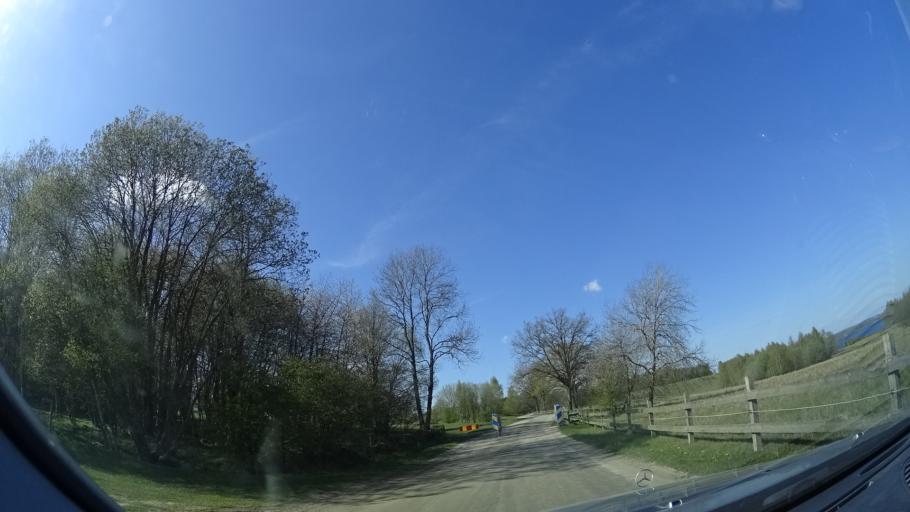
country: SE
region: Skane
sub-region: Hassleholms Kommun
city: Tormestorp
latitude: 56.1079
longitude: 13.6966
